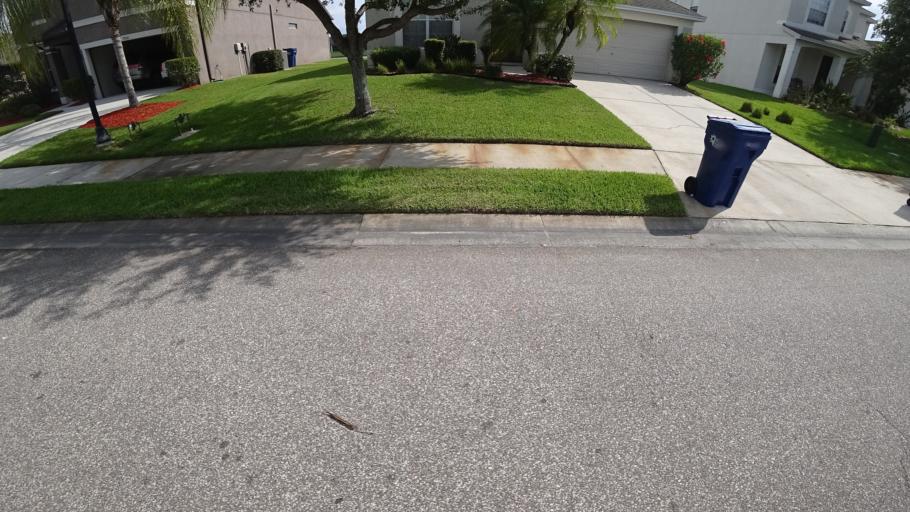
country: US
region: Florida
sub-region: Manatee County
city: Ellenton
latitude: 27.5670
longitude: -82.4661
